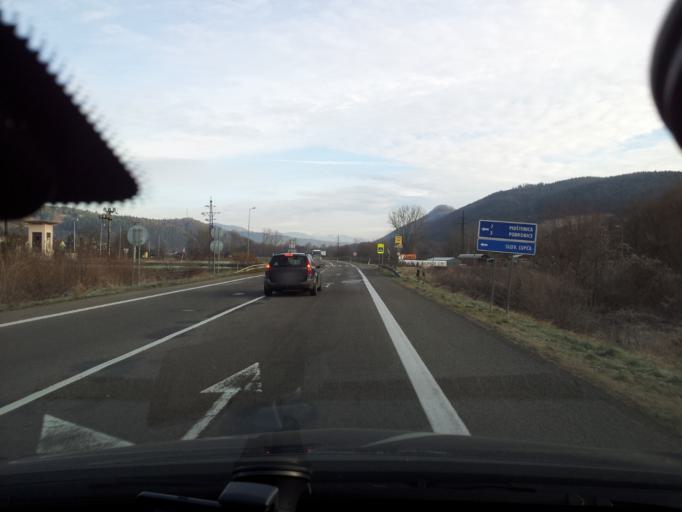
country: SK
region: Banskobystricky
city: Hrochot,Slovakia
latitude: 48.7628
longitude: 19.2777
